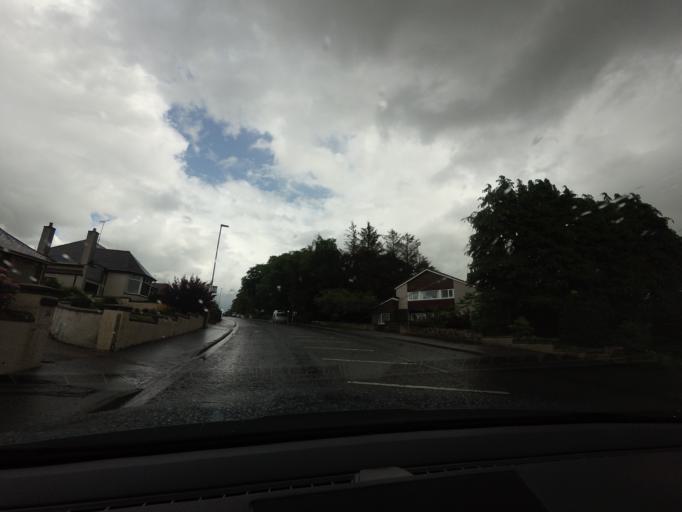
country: GB
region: Scotland
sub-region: Aberdeenshire
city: Turriff
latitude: 57.5405
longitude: -2.4529
